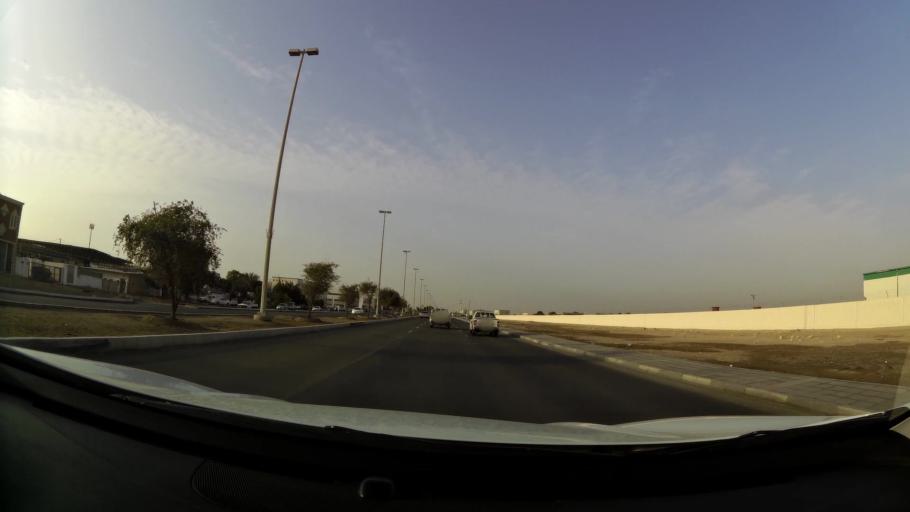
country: AE
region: Abu Dhabi
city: Abu Dhabi
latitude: 24.3508
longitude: 54.5023
